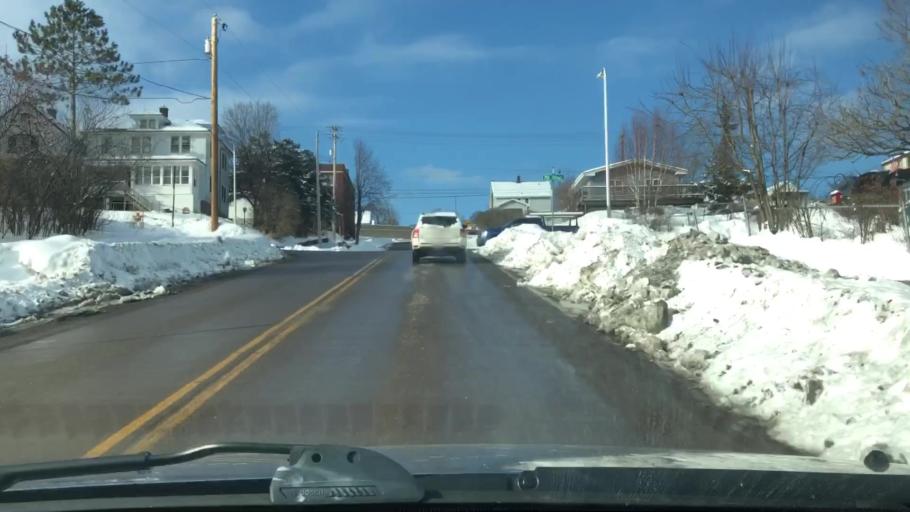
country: US
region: Minnesota
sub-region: Saint Louis County
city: Duluth
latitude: 46.7914
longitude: -92.1053
